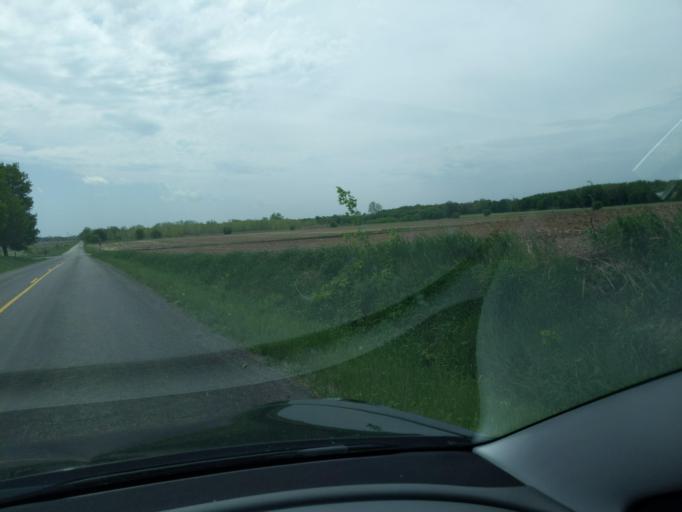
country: US
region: Michigan
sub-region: Ingham County
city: Holt
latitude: 42.5399
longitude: -84.5423
